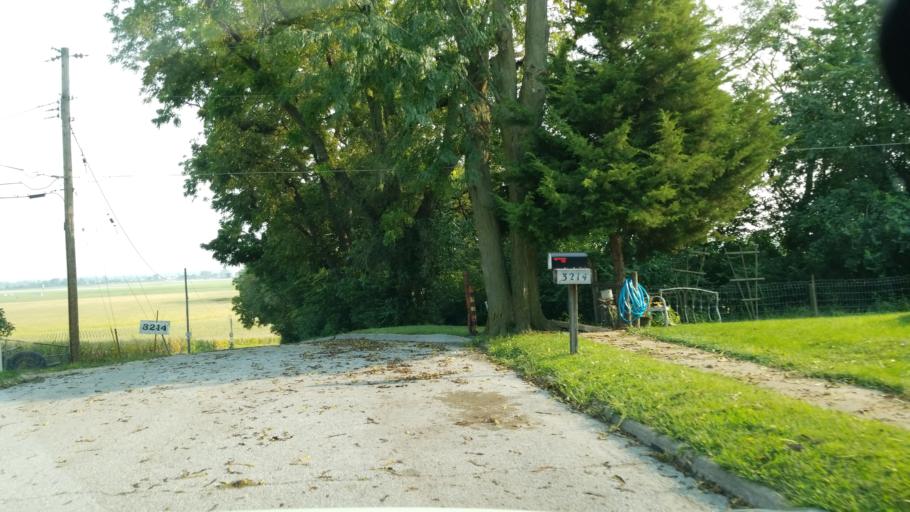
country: US
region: Nebraska
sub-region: Sarpy County
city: Offutt Air Force Base
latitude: 41.1254
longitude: -95.9043
